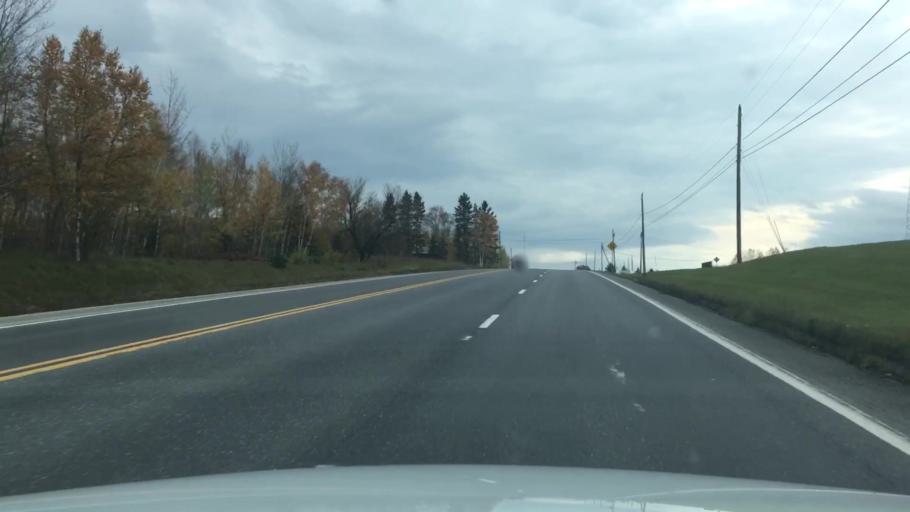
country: US
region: Maine
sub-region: Aroostook County
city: Caribou
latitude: 46.7809
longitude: -67.9891
